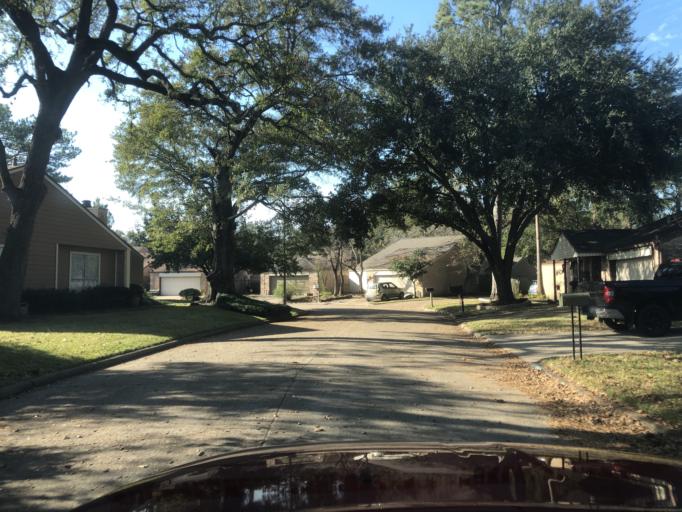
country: US
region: Texas
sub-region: Harris County
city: Spring
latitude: 30.0136
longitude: -95.4608
